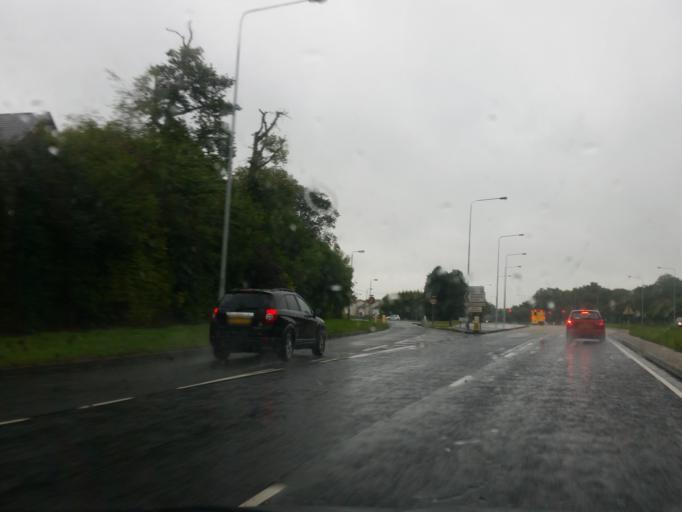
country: GB
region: Northern Ireland
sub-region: North Down District
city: Bangor
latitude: 54.6467
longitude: -5.7168
